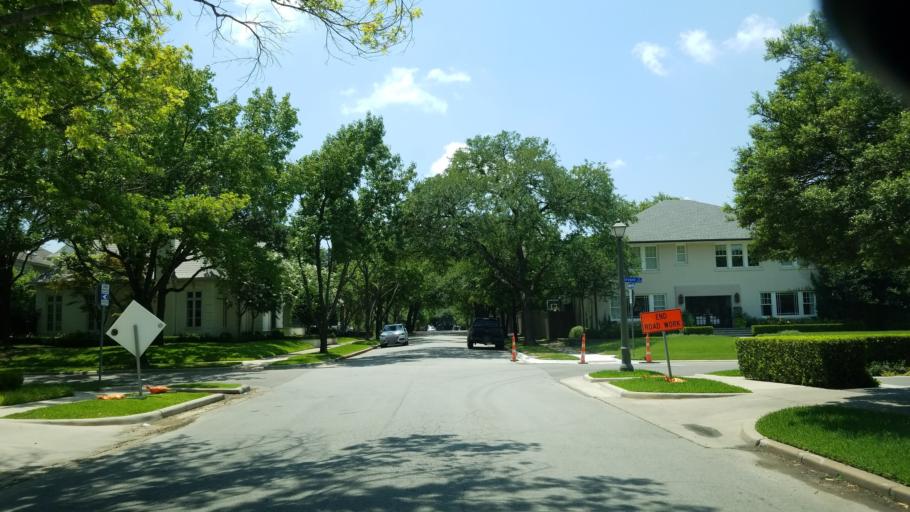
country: US
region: Texas
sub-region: Dallas County
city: Highland Park
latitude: 32.8294
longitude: -96.7891
